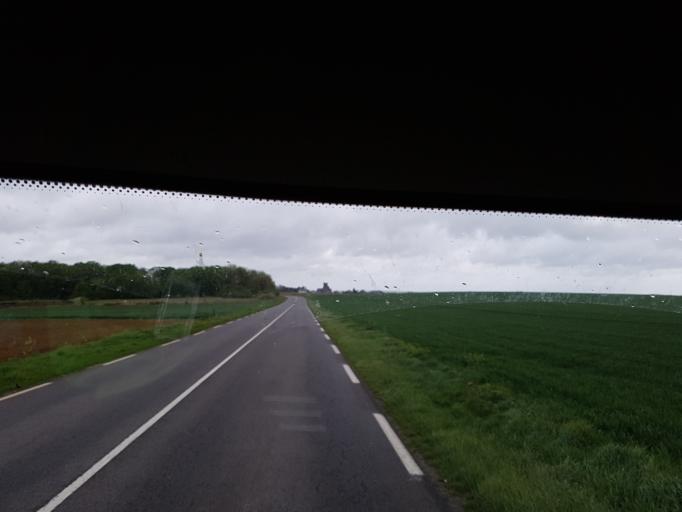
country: FR
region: Picardie
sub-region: Departement de l'Aisne
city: Crouy
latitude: 49.4355
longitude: 3.3547
